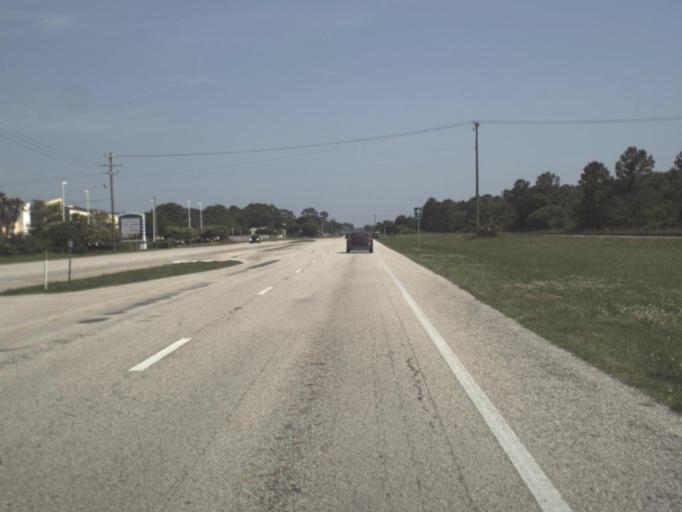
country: US
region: Florida
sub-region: Saint Johns County
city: Villano Beach
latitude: 29.9559
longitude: -81.3446
